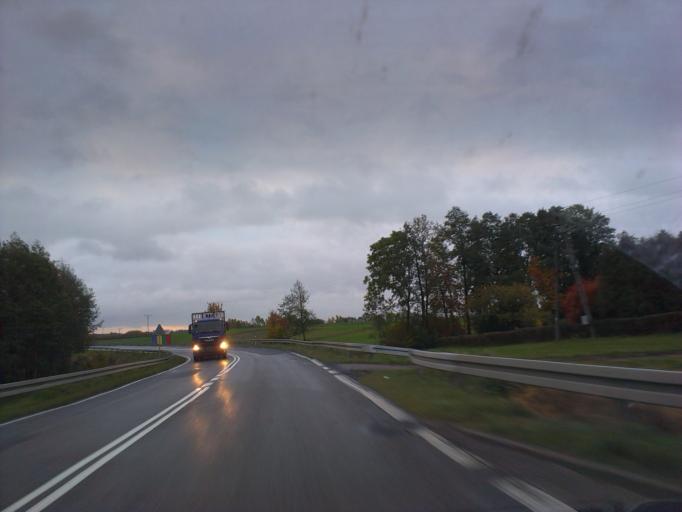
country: PL
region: Kujawsko-Pomorskie
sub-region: Powiat tucholski
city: Lubiewo
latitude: 53.5083
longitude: 17.9765
